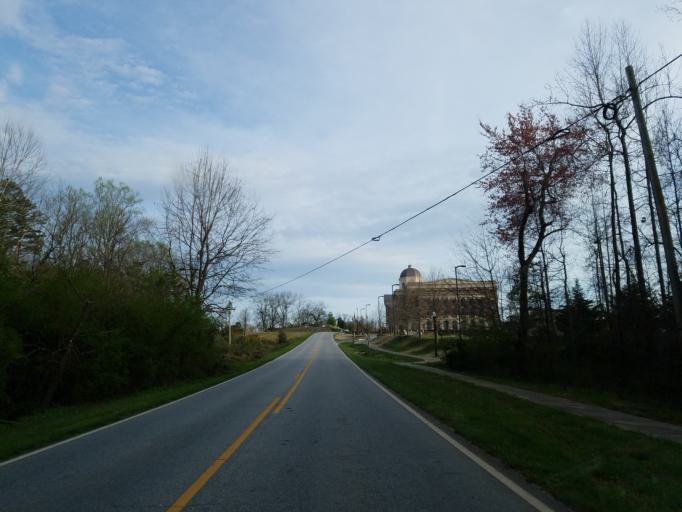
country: US
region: Georgia
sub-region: Dawson County
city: Dawsonville
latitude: 34.4253
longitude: -84.1199
